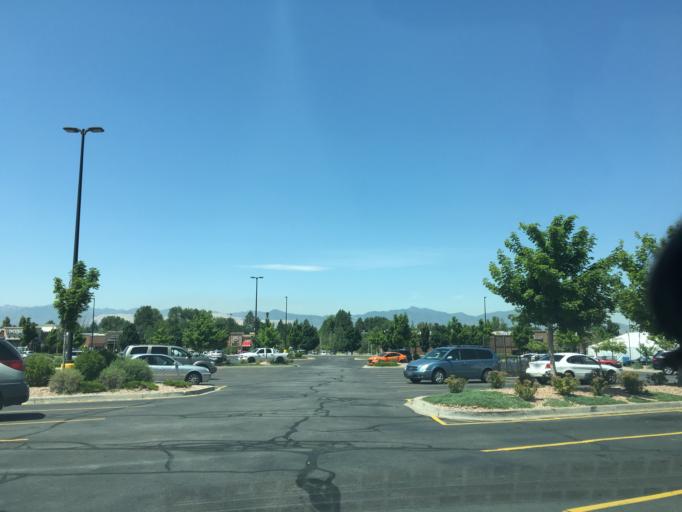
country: US
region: Utah
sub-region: Salt Lake County
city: Sandy Hills
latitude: 40.5855
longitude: -111.8609
